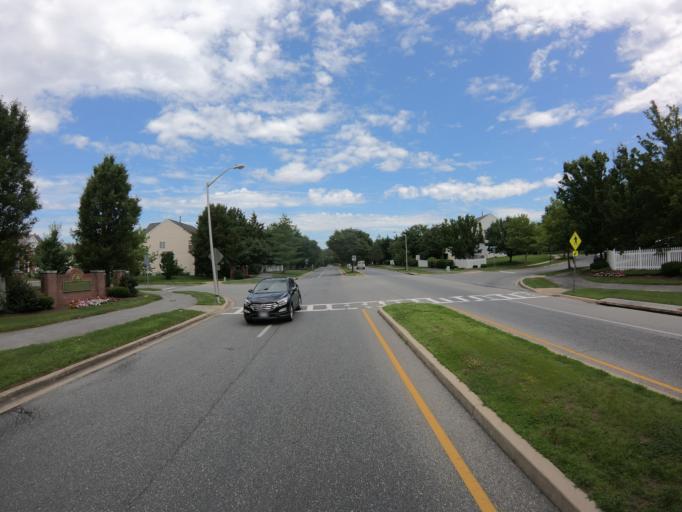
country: US
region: Maryland
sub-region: Prince George's County
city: Lanham
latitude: 38.9814
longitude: -76.8677
